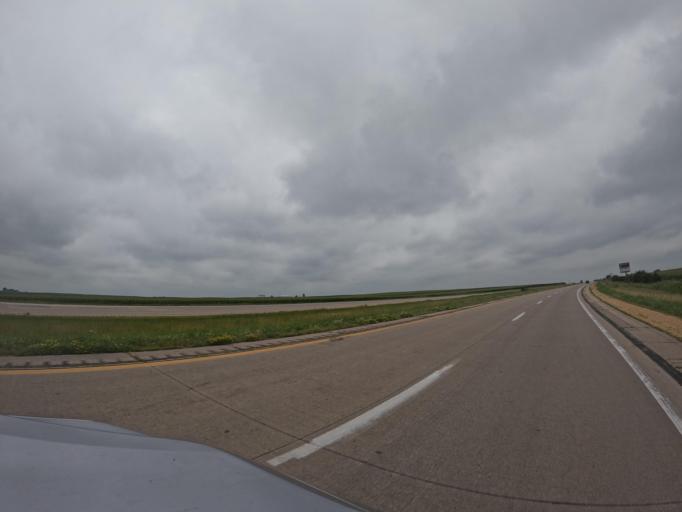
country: US
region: Iowa
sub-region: Clinton County
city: De Witt
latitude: 41.9076
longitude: -90.5908
